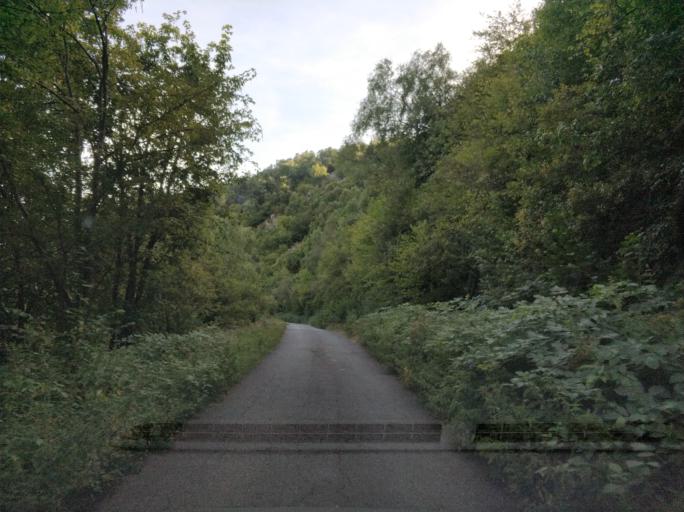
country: IT
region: Piedmont
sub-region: Provincia di Torino
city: Monastero di Lanzo
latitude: 45.3228
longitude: 7.4198
